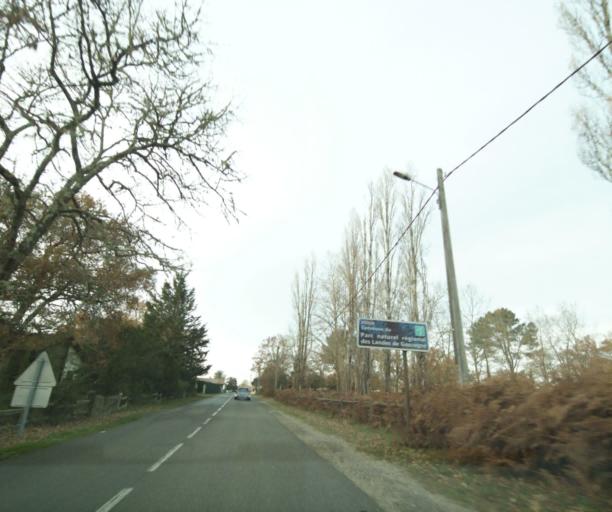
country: FR
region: Aquitaine
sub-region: Departement de la Gironde
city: Prechac
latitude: 44.2856
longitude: -0.2549
